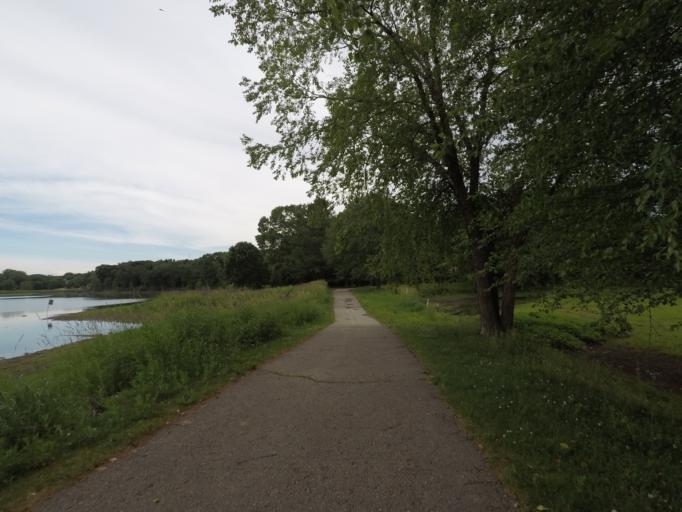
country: US
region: Wisconsin
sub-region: Dane County
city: Middleton
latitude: 43.0881
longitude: -89.5121
